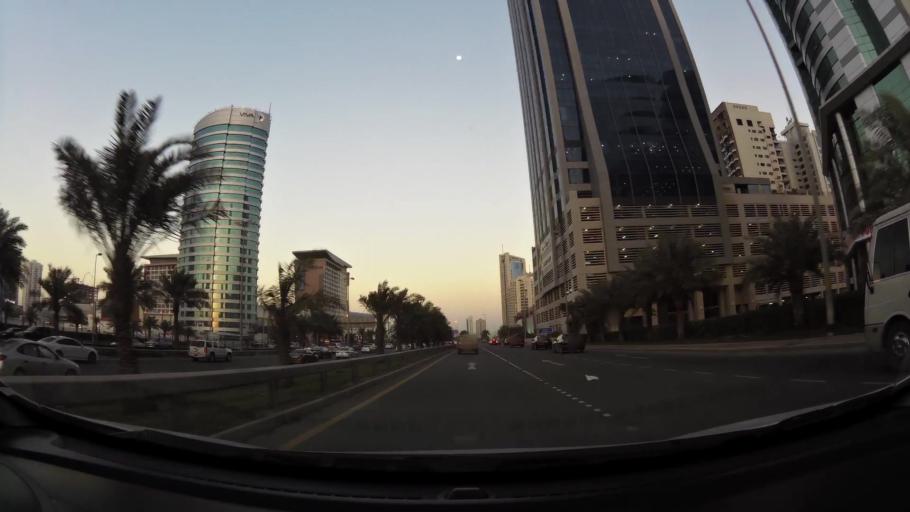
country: BH
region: Manama
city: Jidd Hafs
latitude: 26.2314
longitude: 50.5494
